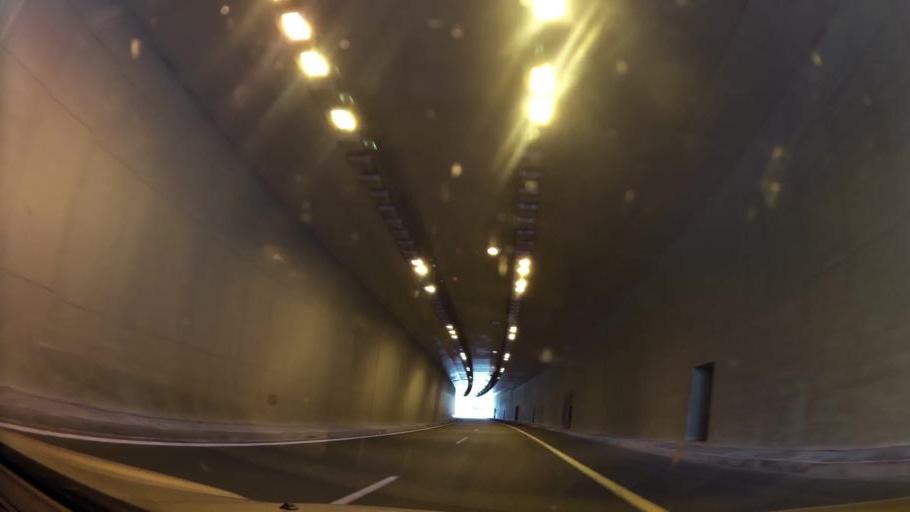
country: GR
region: Central Macedonia
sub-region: Nomos Imathias
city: Rizomata
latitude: 40.3914
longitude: 22.1561
